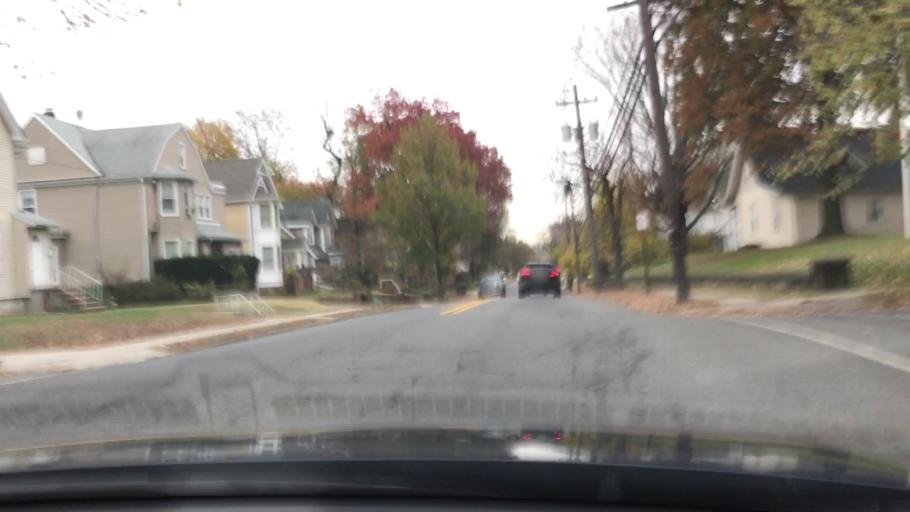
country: US
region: New Jersey
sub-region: Bergen County
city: Rutherford
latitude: 40.8348
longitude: -74.1111
